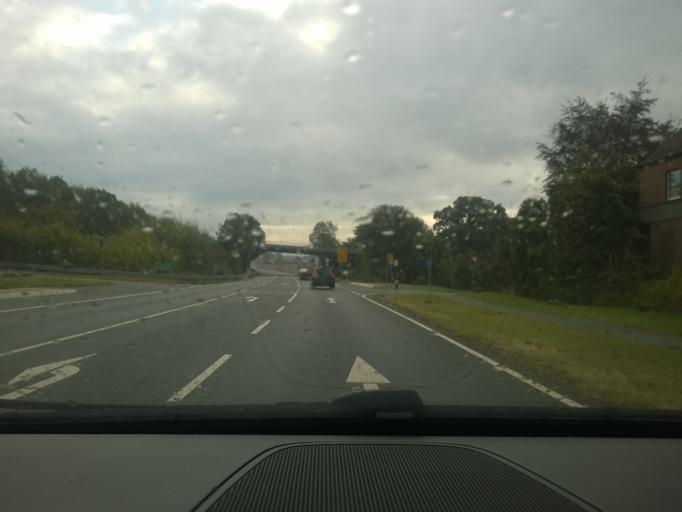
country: DE
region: North Rhine-Westphalia
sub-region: Regierungsbezirk Munster
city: Billerbeck
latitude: 51.9352
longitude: 7.2592
